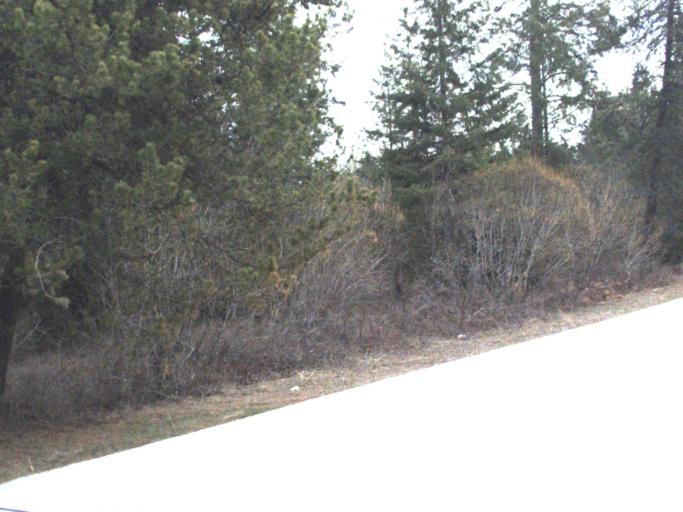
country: US
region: Washington
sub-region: Pend Oreille County
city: Newport
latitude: 48.2261
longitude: -117.1355
